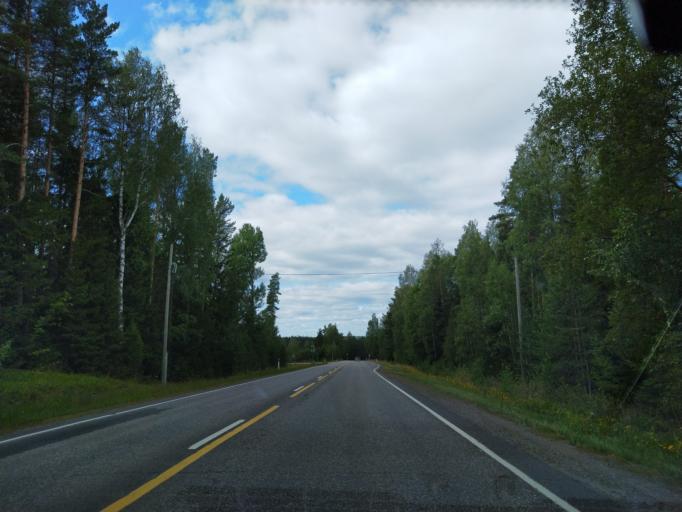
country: FI
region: Haeme
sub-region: Riihimaeki
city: Loppi
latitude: 60.7247
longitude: 24.4167
